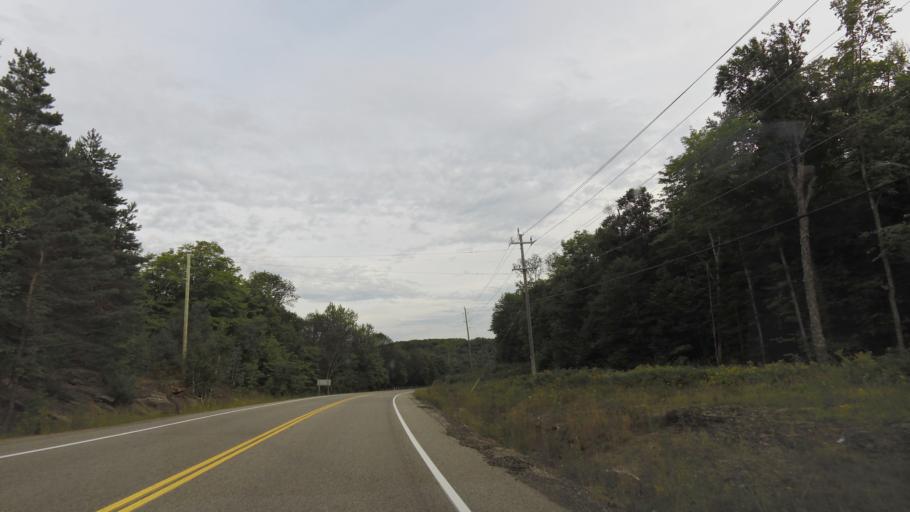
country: CA
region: Ontario
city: Bancroft
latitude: 45.0378
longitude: -78.4603
